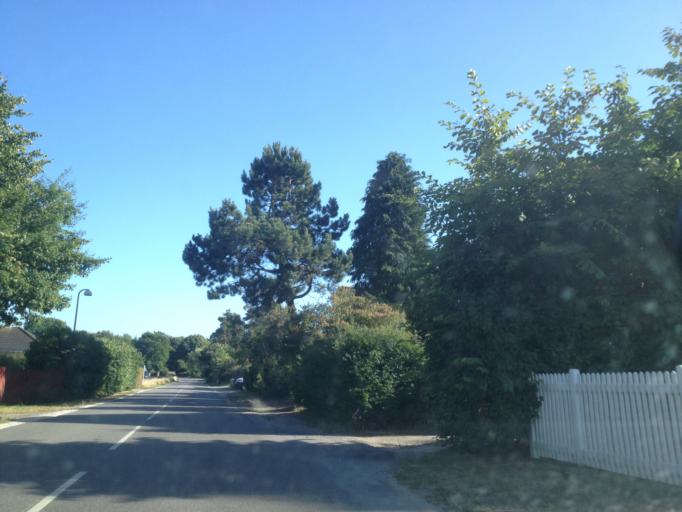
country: DK
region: Capital Region
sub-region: Gribskov Kommune
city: Helsinge
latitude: 56.0500
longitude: 12.1095
